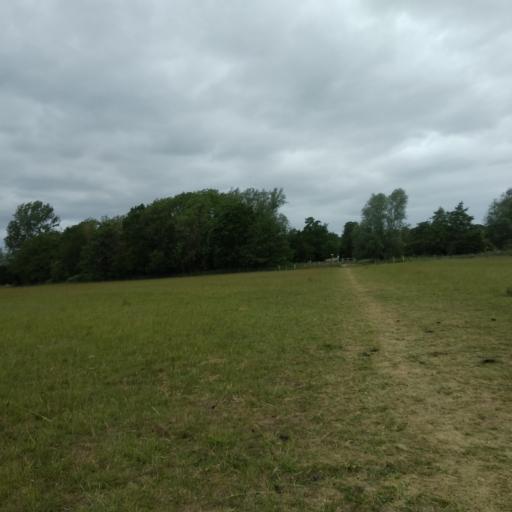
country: GB
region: England
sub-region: Kent
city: Ashford
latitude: 51.1553
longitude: 0.8276
